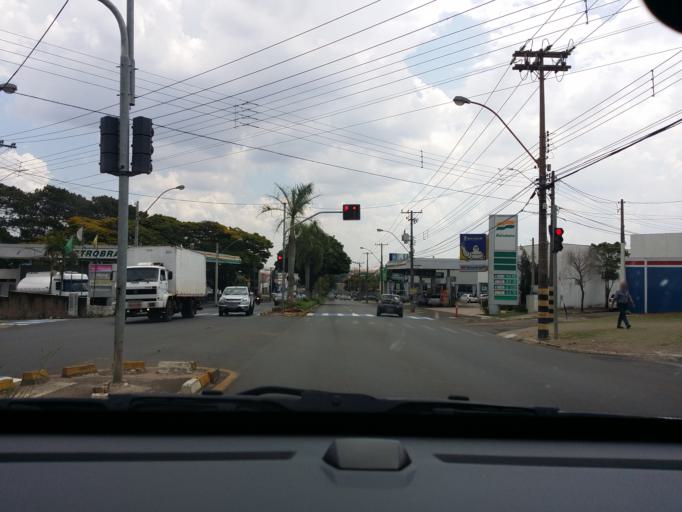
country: BR
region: Sao Paulo
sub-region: Sao Carlos
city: Sao Carlos
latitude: -22.0330
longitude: -47.8834
